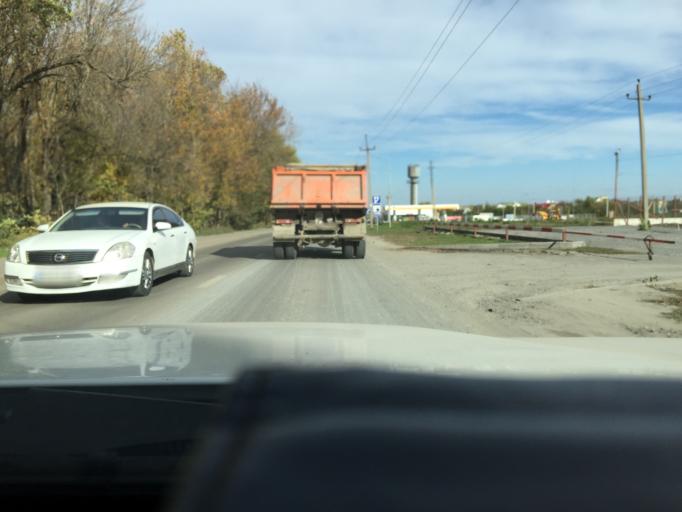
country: RU
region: Rostov
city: Imeni Chkalova
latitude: 47.2962
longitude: 39.8036
